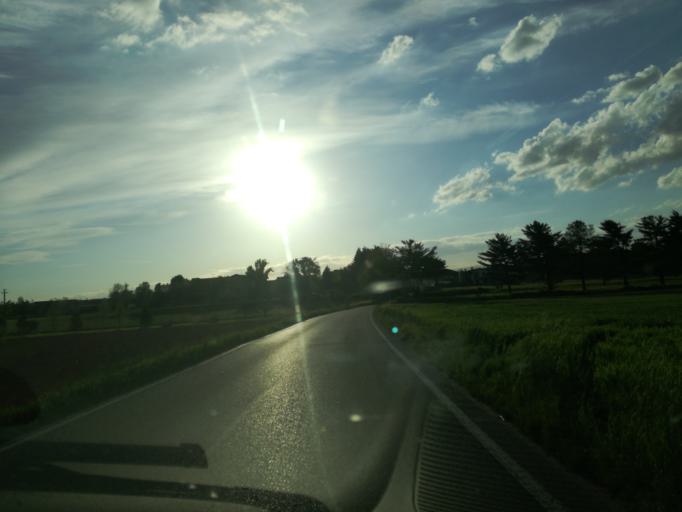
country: IT
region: Lombardy
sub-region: Provincia di Monza e Brianza
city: Ronco Briantino
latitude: 45.6757
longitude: 9.4149
